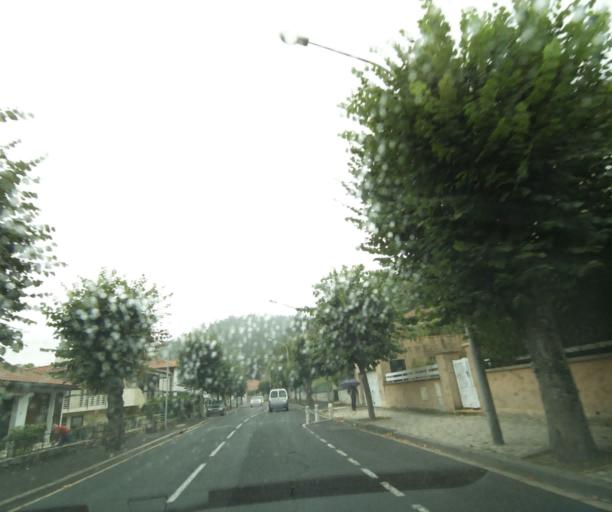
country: FR
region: Auvergne
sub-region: Departement du Puy-de-Dome
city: Ceyrat
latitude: 45.7278
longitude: 3.0638
